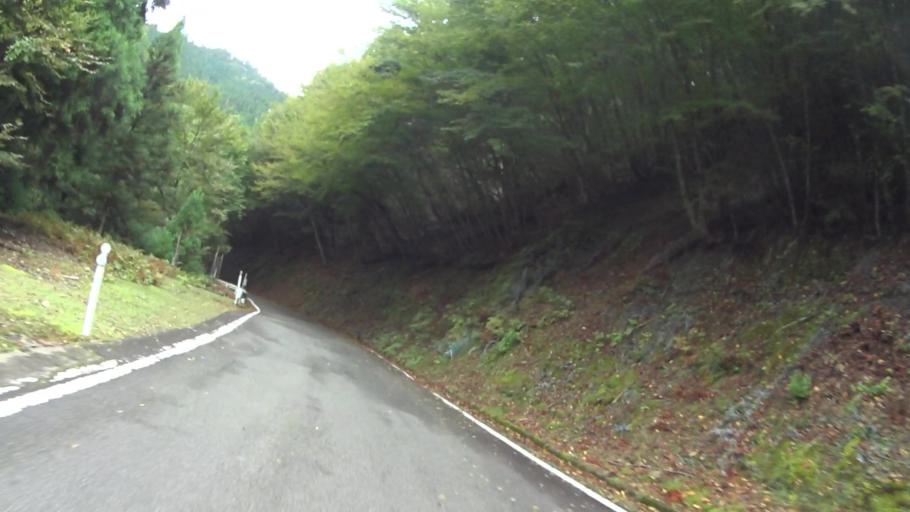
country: JP
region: Fukui
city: Obama
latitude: 35.2765
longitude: 135.7191
